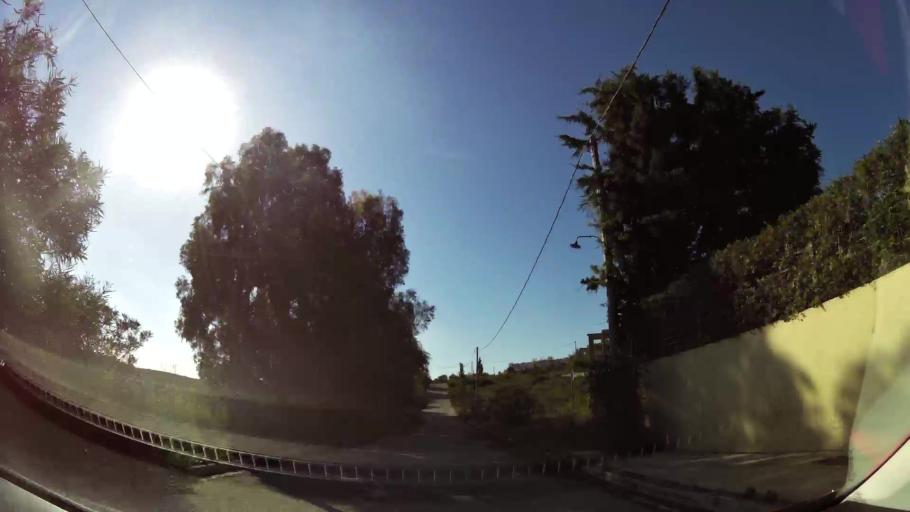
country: GR
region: Attica
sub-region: Nomarchia Anatolikis Attikis
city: Dhrafi
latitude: 38.0201
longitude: 23.9005
